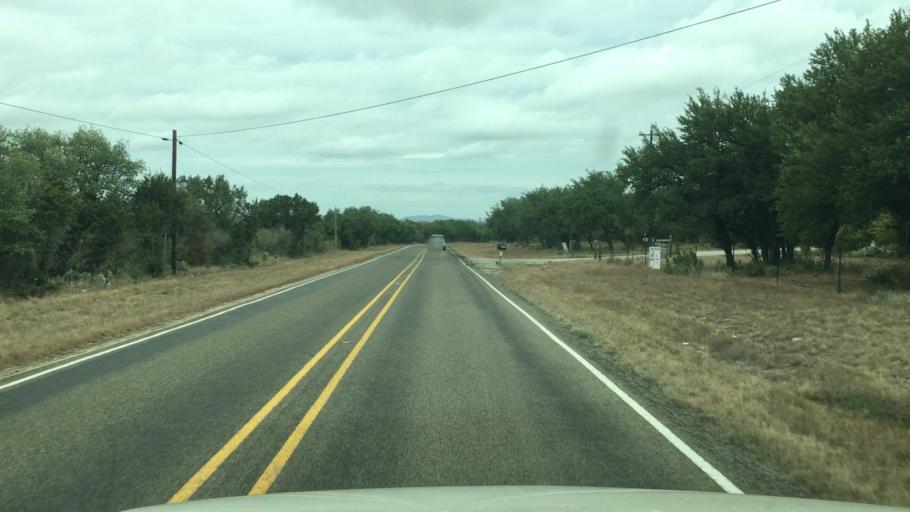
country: US
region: Texas
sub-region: Llano County
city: Horseshoe Bay
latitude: 30.4710
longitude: -98.4145
